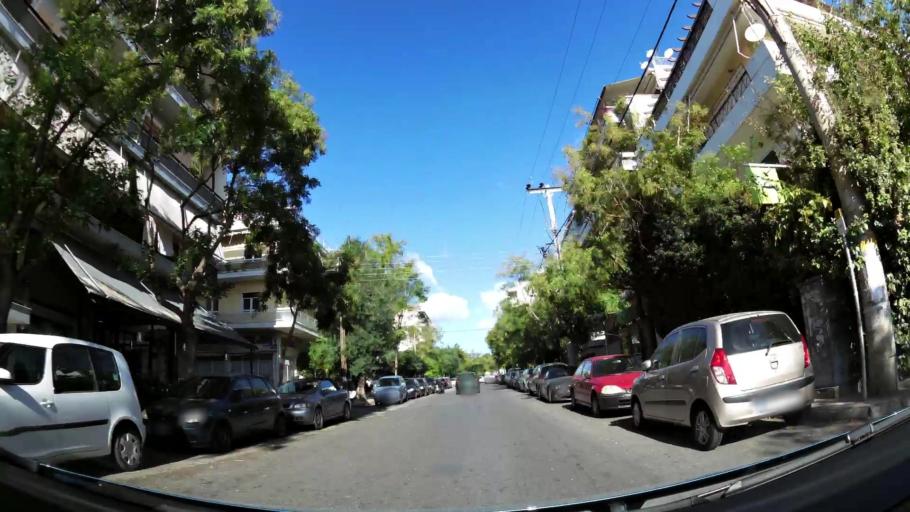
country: GR
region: Attica
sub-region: Nomarchia Athinas
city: Neo Psychiko
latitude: 37.9982
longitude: 23.7754
